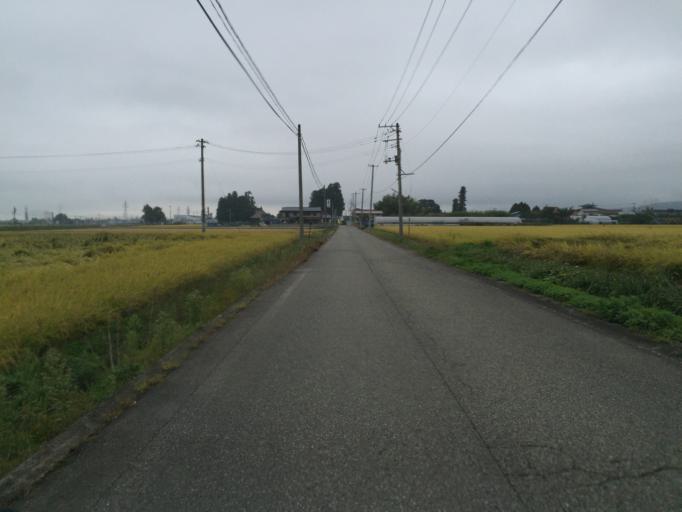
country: JP
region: Fukushima
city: Kitakata
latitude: 37.4460
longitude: 139.9148
